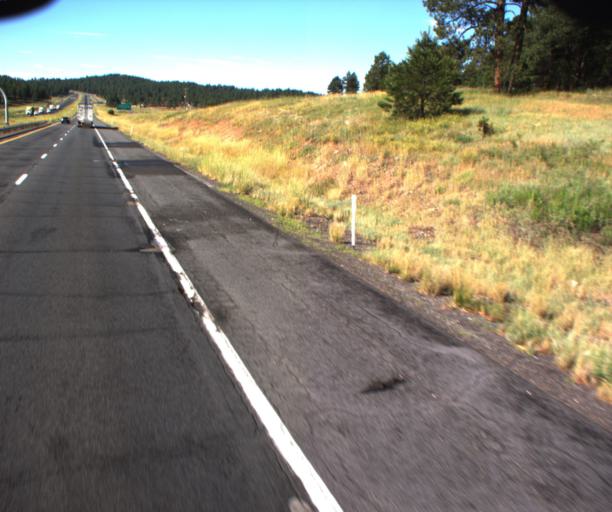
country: US
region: Arizona
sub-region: Coconino County
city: Kachina Village
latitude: 35.1023
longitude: -111.6820
